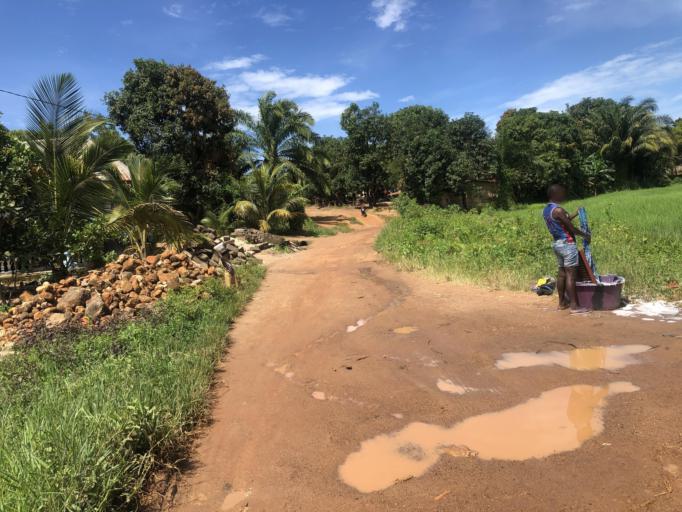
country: SL
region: Eastern Province
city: Koidu
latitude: 8.6407
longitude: -10.9494
